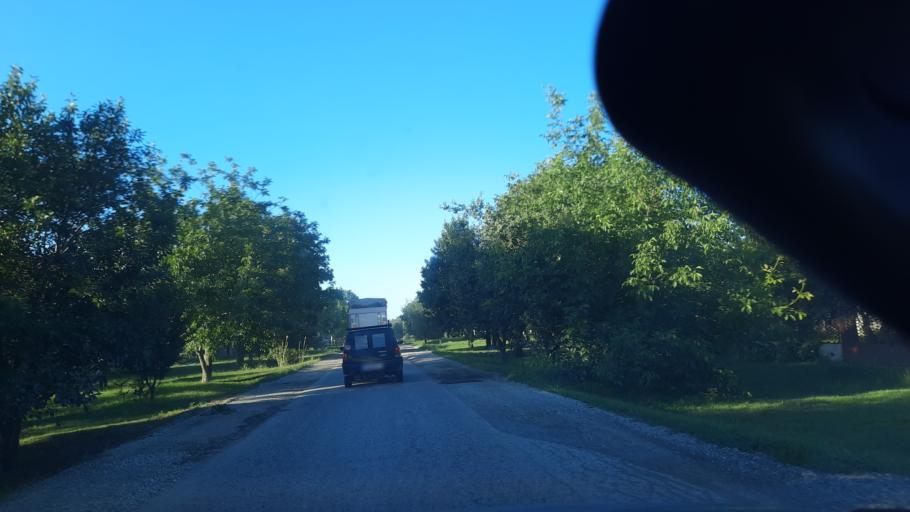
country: RS
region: Autonomna Pokrajina Vojvodina
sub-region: Sremski Okrug
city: Irig
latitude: 45.1132
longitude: 19.9341
